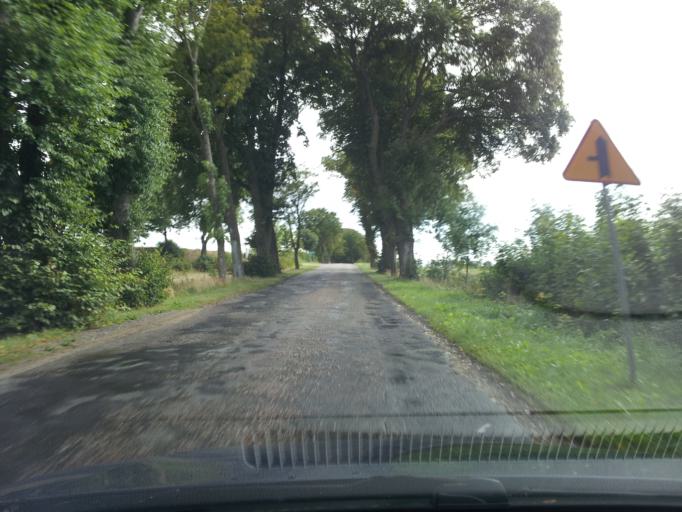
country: PL
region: Kujawsko-Pomorskie
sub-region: Powiat brodnicki
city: Gorzno
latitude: 53.2138
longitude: 19.6351
